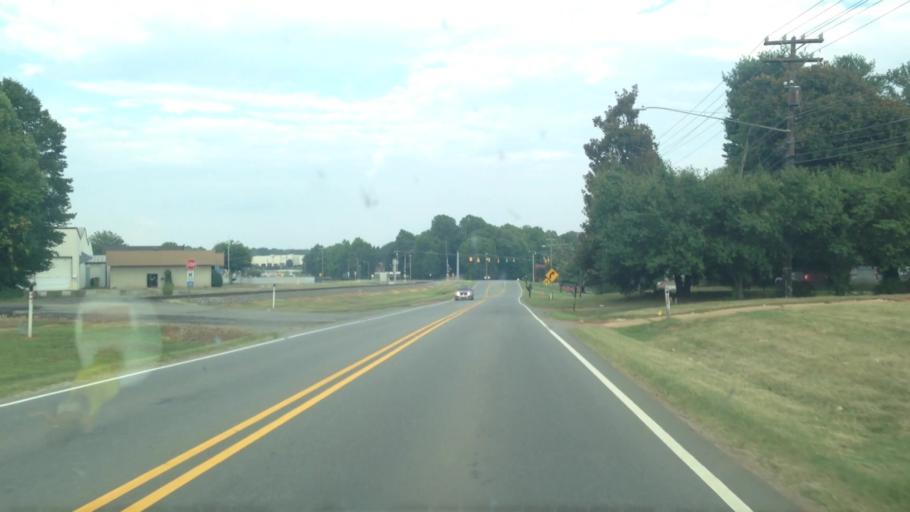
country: US
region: North Carolina
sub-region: Forsyth County
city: Kernersville
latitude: 36.1356
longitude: -80.0990
